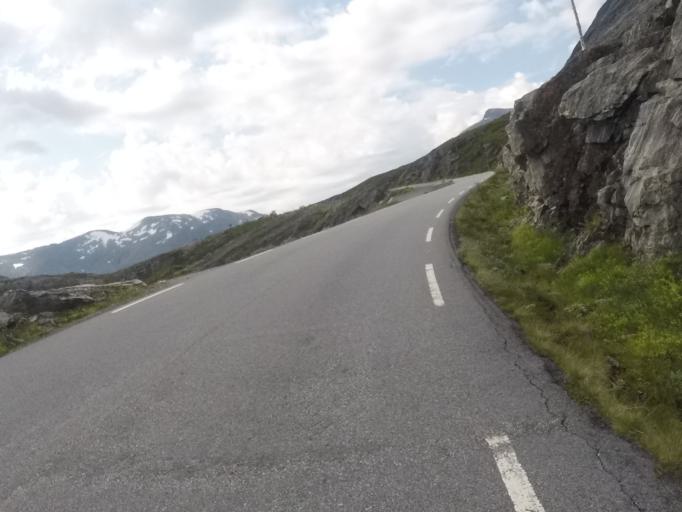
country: NO
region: More og Romsdal
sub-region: Rauma
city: Andalsnes
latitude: 62.4348
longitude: 7.6600
